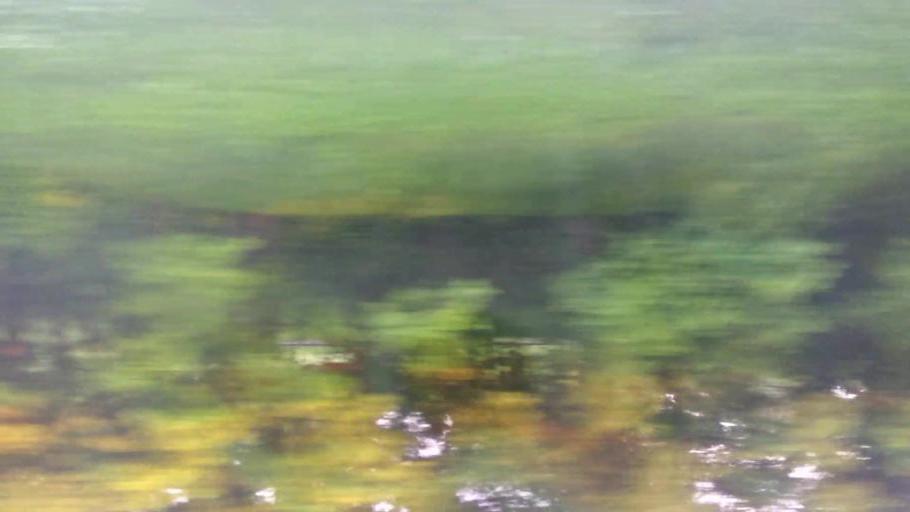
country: RU
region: Moskovskaya
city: Barybino
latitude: 55.2845
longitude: 37.8895
